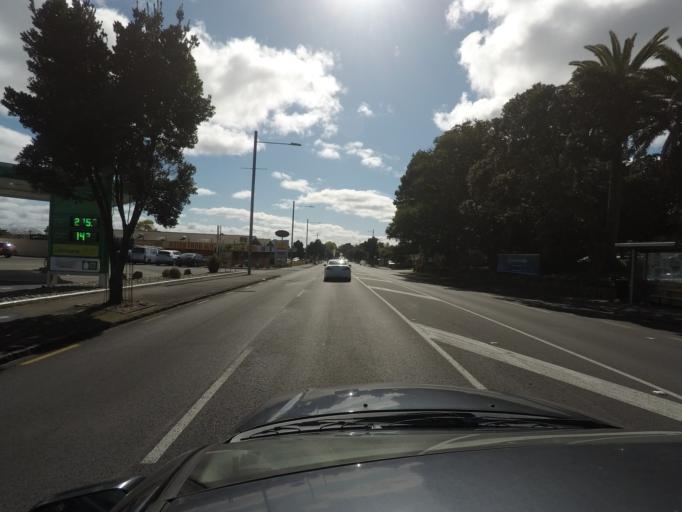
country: NZ
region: Auckland
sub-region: Auckland
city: Rosebank
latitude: -36.8887
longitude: 174.7108
